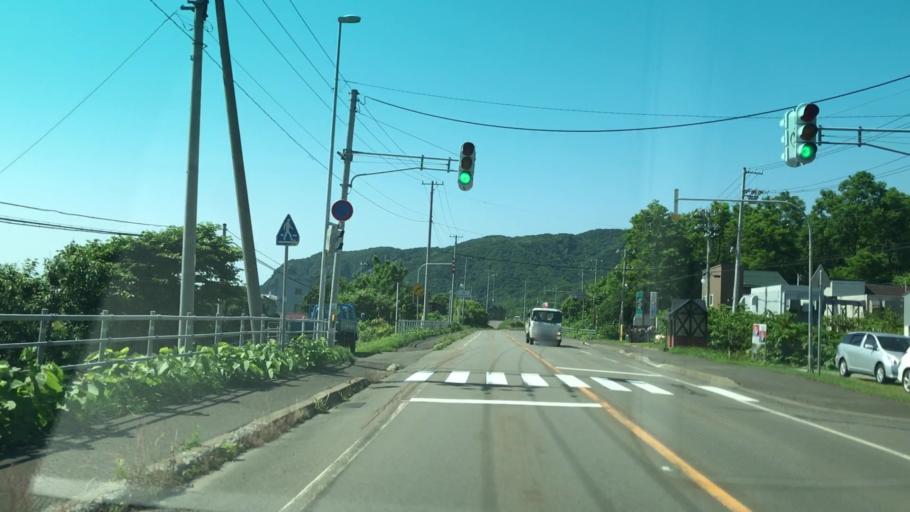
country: JP
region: Hokkaido
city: Iwanai
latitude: 43.0706
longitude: 140.4910
